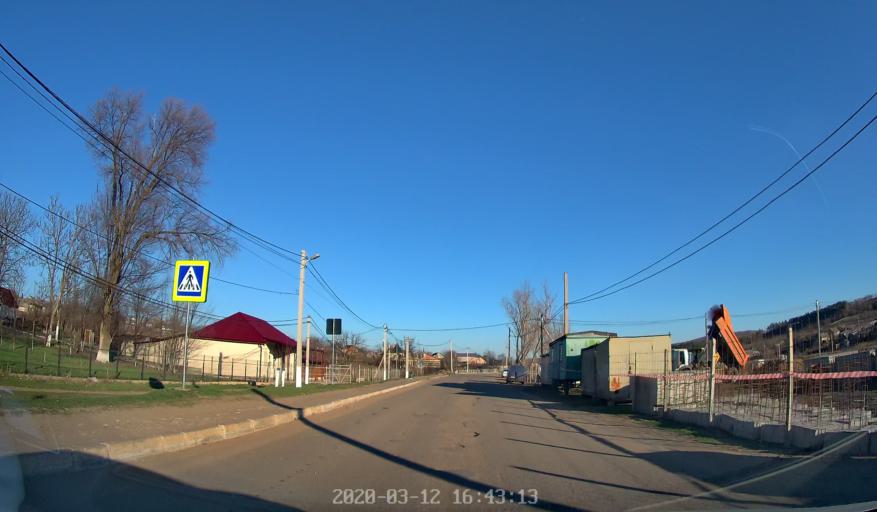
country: MD
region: Anenii Noi
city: Anenii Noi
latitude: 46.8207
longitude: 29.1393
